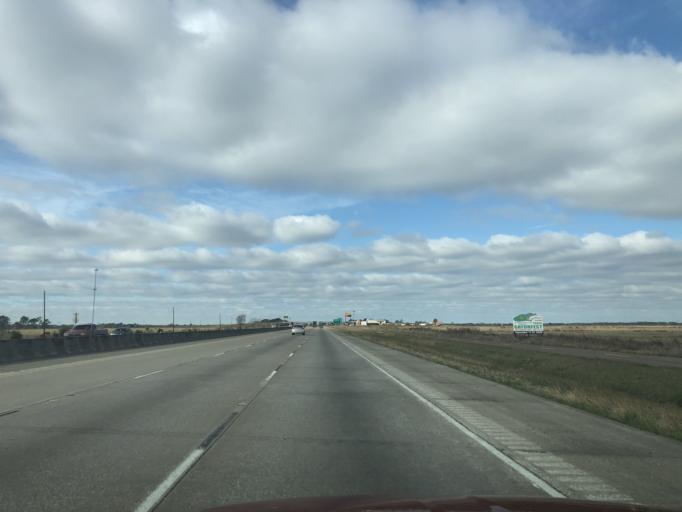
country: US
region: Texas
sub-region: Chambers County
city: Winnie
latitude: 29.8343
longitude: -94.5313
